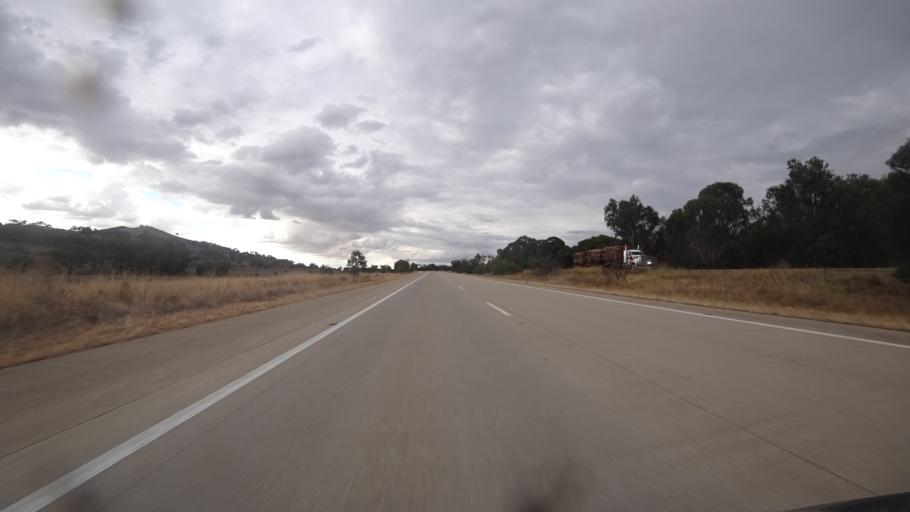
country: AU
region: New South Wales
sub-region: Yass Valley
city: Yass
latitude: -34.7980
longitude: 148.6944
